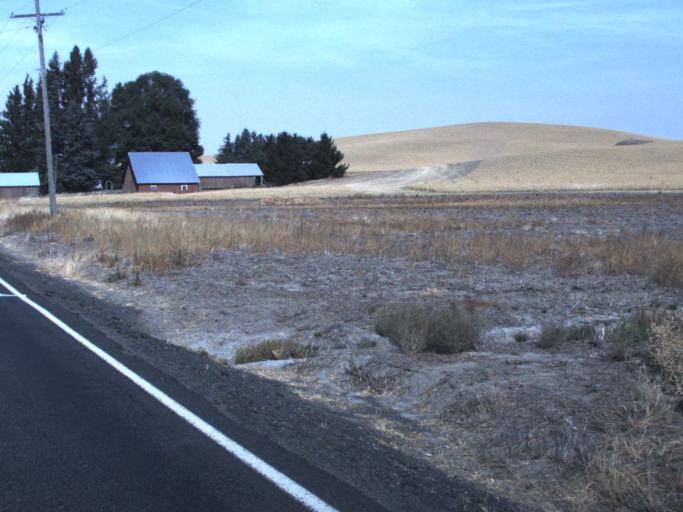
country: US
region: Washington
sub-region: Whitman County
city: Colfax
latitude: 47.0801
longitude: -117.1548
